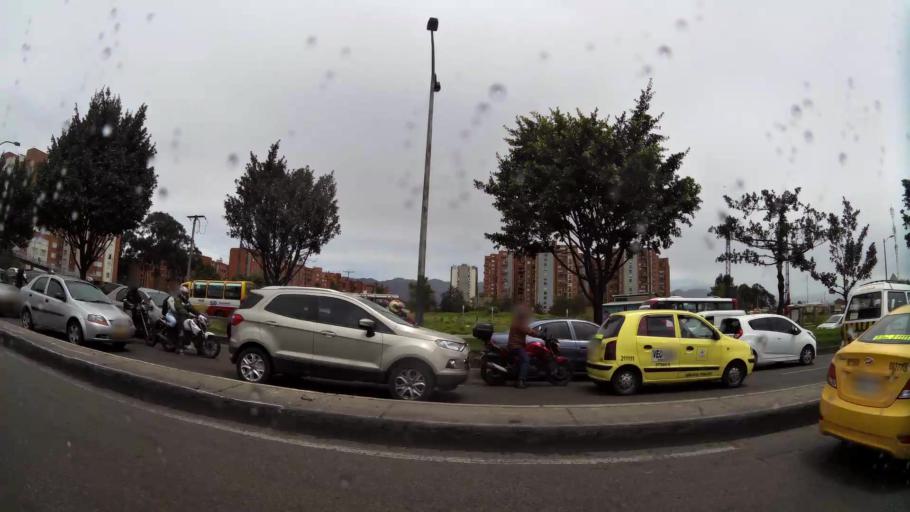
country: CO
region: Bogota D.C.
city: Bogota
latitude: 4.6463
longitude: -74.1094
